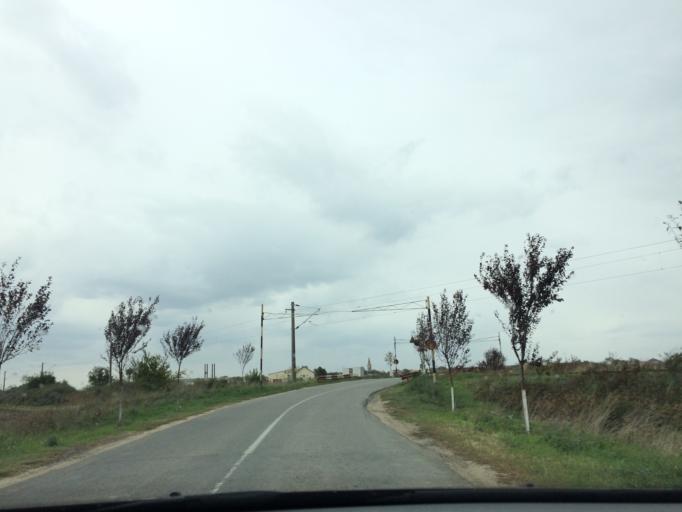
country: RO
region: Timis
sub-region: Oras Recas
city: Recas
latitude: 45.7908
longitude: 21.5111
